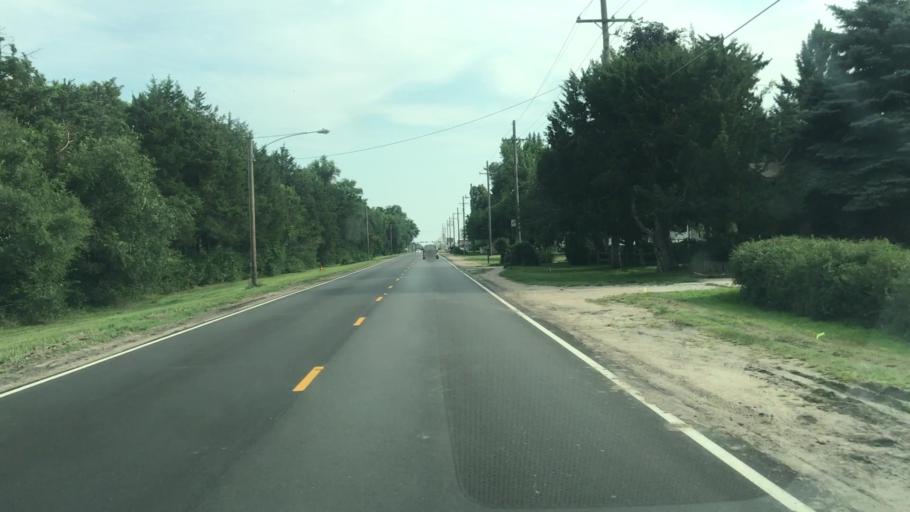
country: US
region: Nebraska
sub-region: Hall County
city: Grand Island
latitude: 40.9504
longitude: -98.3788
